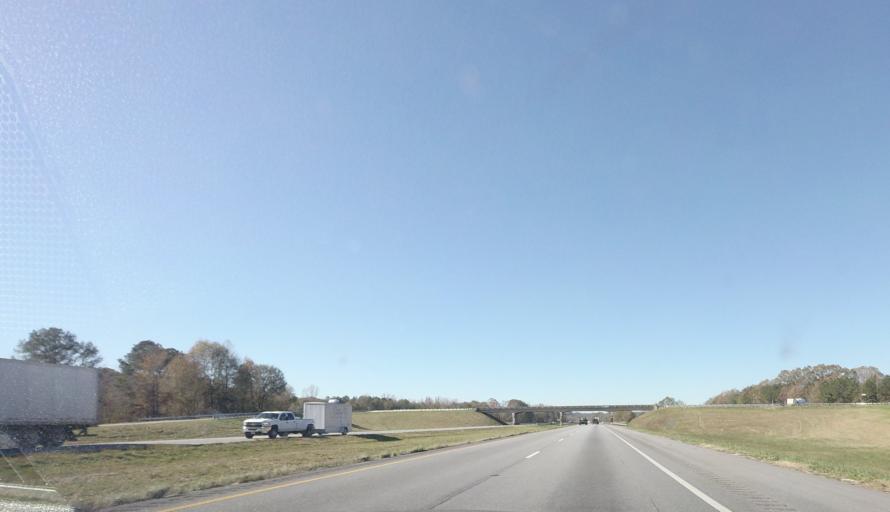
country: US
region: Alabama
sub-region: Calhoun County
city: Choccolocco
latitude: 33.6180
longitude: -85.7209
